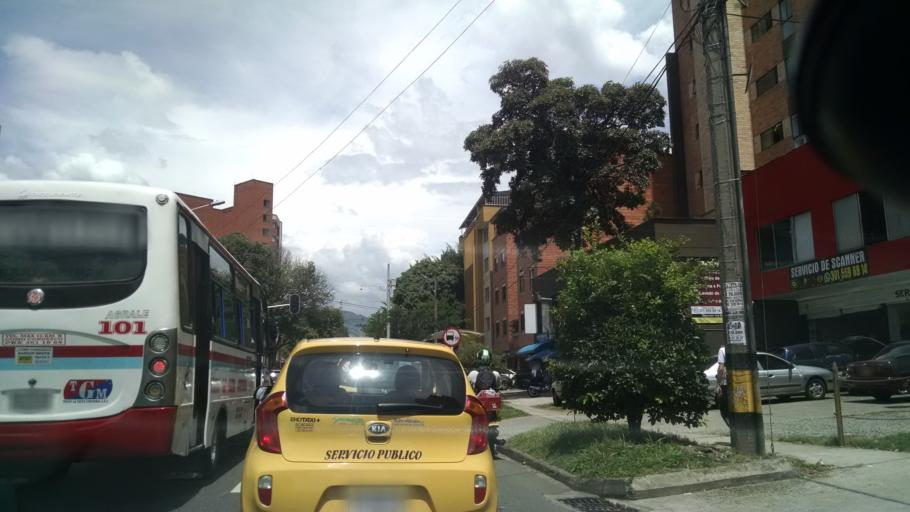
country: CO
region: Antioquia
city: Medellin
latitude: 6.2415
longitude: -75.5831
